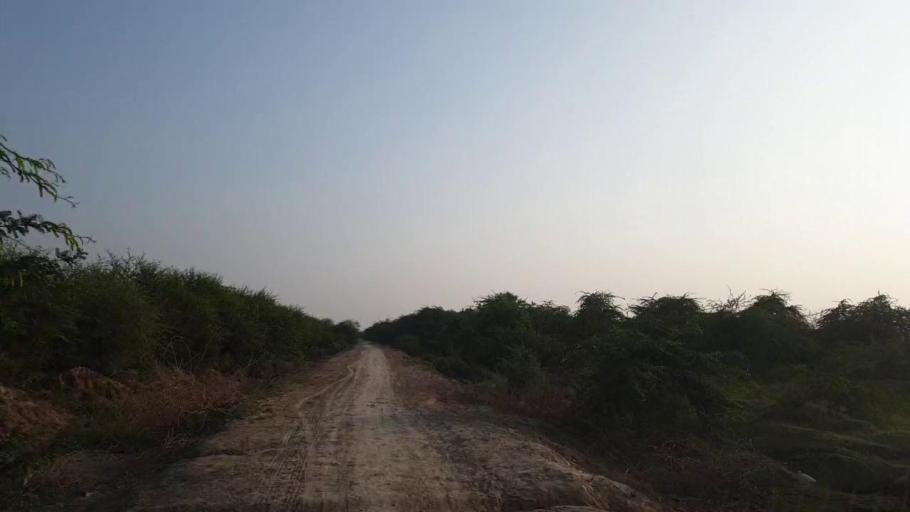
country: PK
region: Sindh
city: Kario
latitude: 24.8749
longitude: 68.6205
